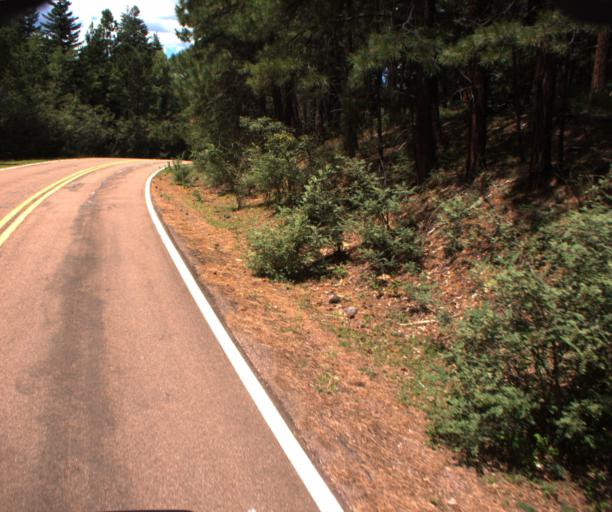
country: US
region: Arizona
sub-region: Navajo County
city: Pinetop-Lakeside
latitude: 34.0286
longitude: -109.7672
